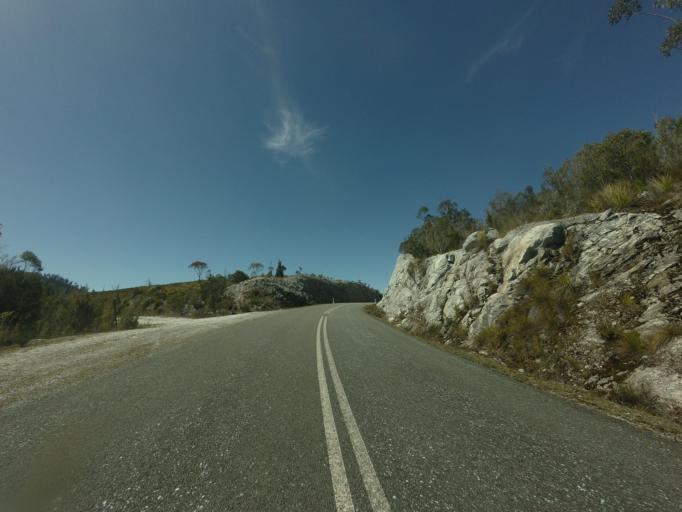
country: AU
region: Tasmania
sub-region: Huon Valley
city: Geeveston
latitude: -42.8466
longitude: 146.2397
